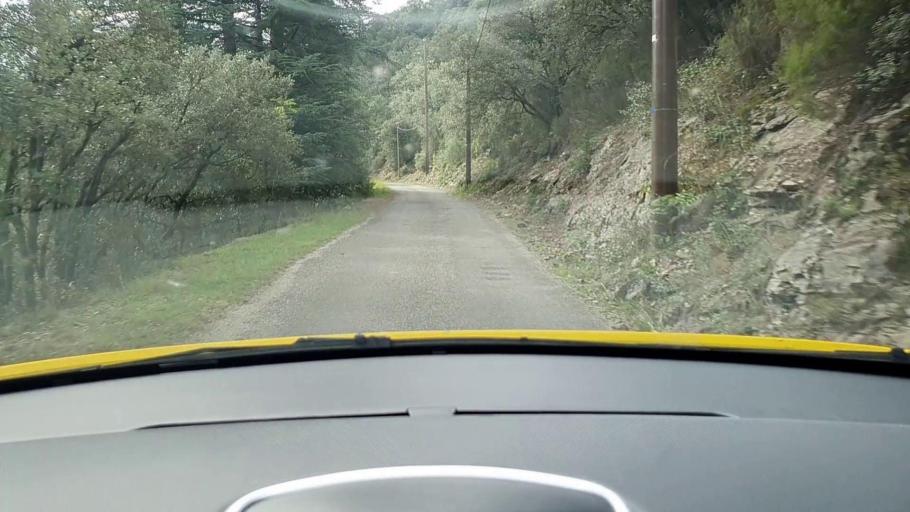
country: FR
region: Languedoc-Roussillon
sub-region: Departement du Gard
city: Sumene
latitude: 44.0117
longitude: 3.6596
